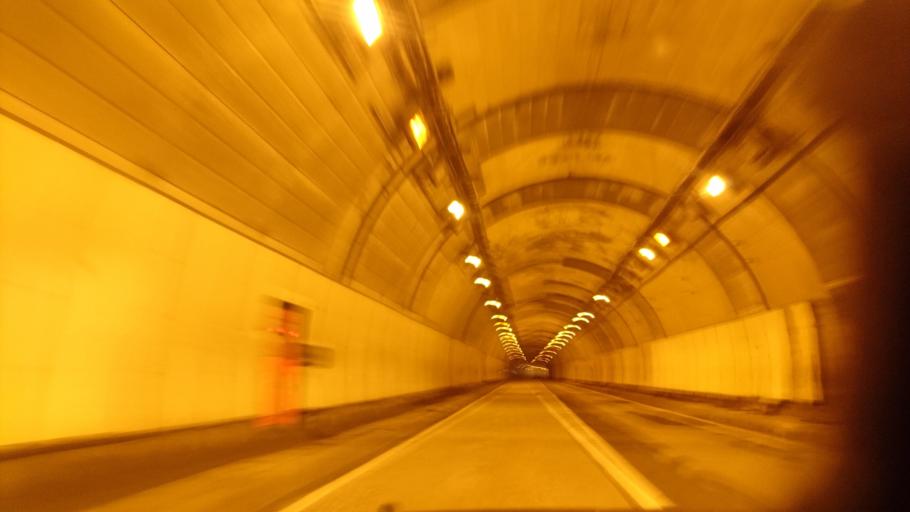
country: JP
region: Iwate
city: Shizukuishi
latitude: 39.6922
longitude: 140.7968
